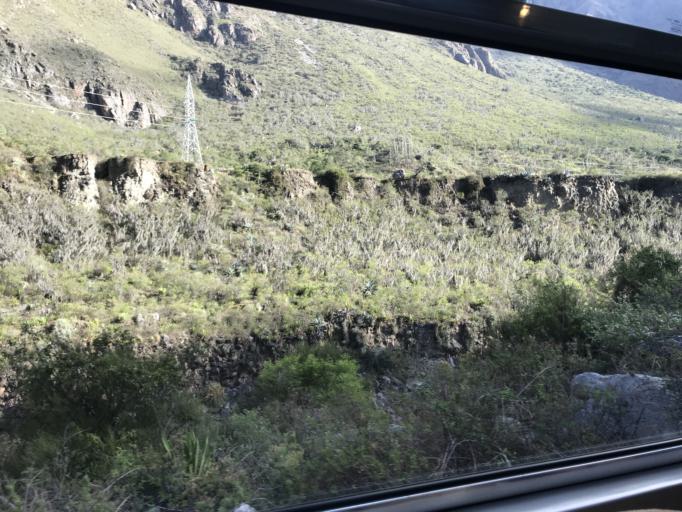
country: PE
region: Cusco
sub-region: Provincia de Urubamba
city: Ollantaytambo
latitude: -13.2204
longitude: -72.3916
